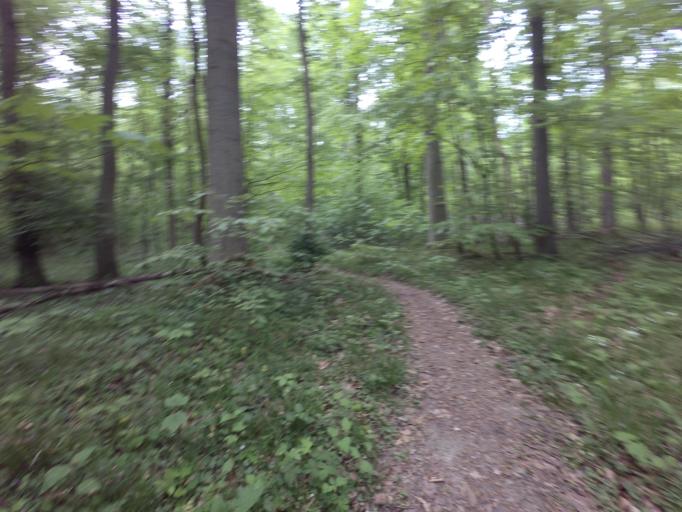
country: DE
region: Lower Saxony
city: Diekholzen
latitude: 52.1156
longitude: 9.9070
